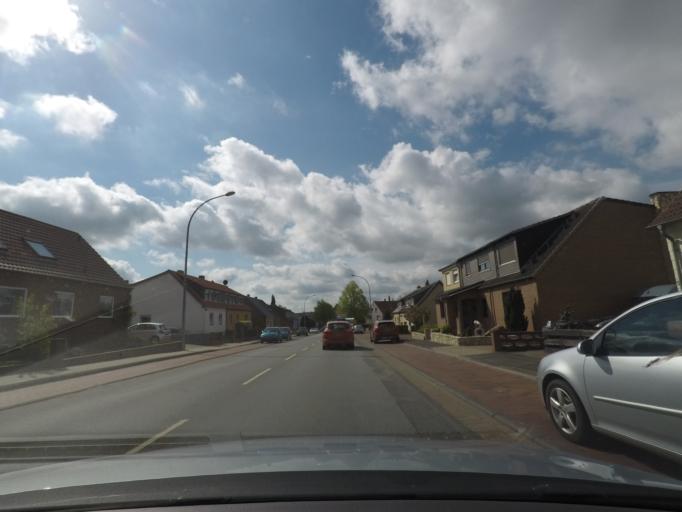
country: DE
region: Lower Saxony
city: Helmstedt
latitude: 52.2405
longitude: 10.9996
